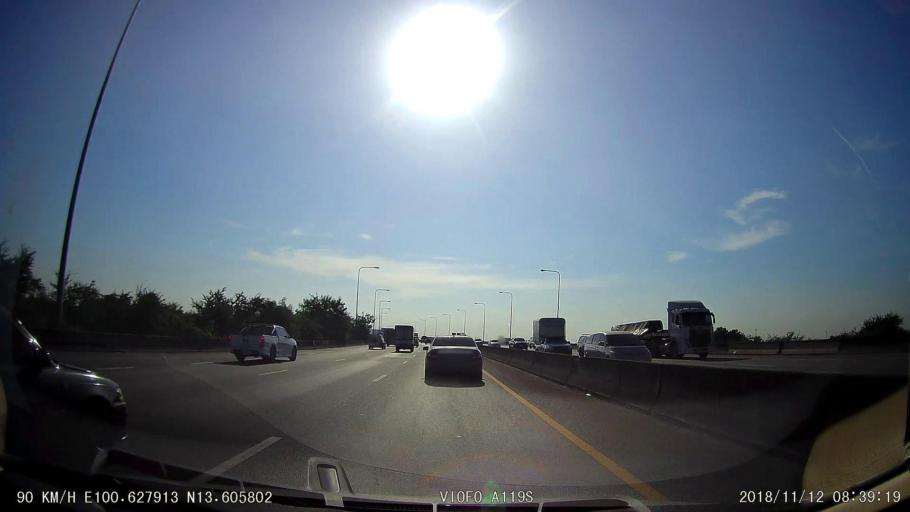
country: TH
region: Samut Prakan
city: Samut Prakan
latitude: 13.6056
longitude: 100.6282
